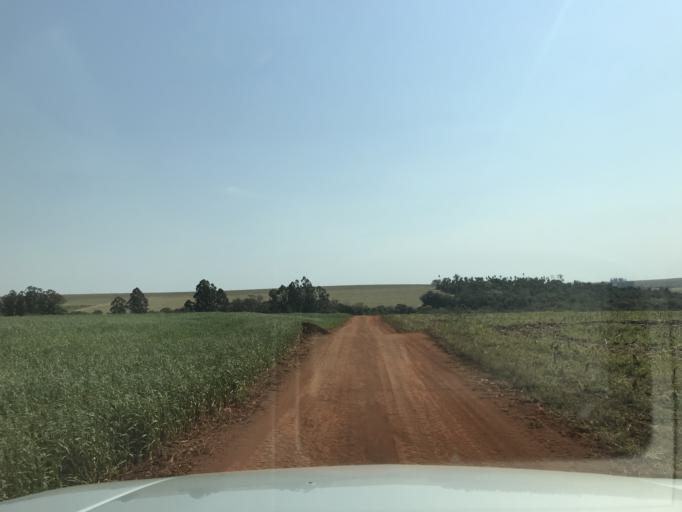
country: BR
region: Parana
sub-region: Palotina
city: Palotina
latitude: -24.2262
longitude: -53.7385
